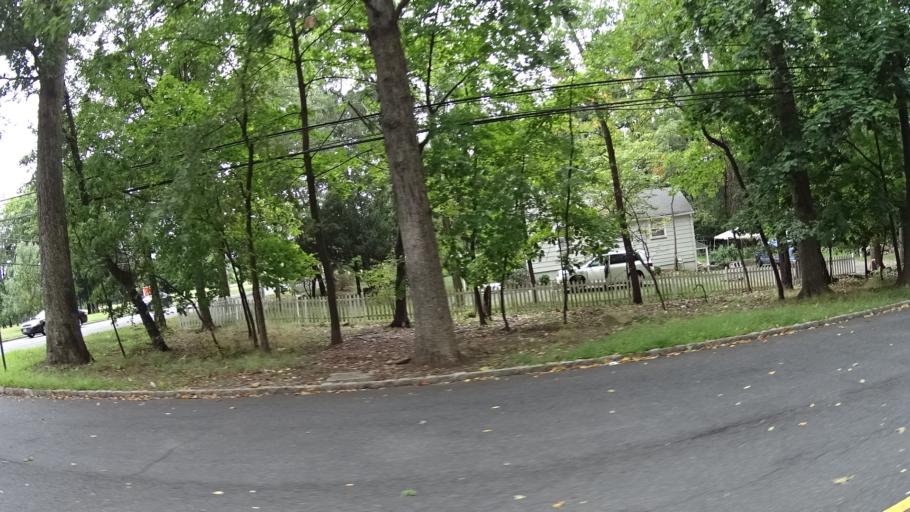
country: US
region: New Jersey
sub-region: Union County
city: New Providence
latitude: 40.6838
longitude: -74.4069
